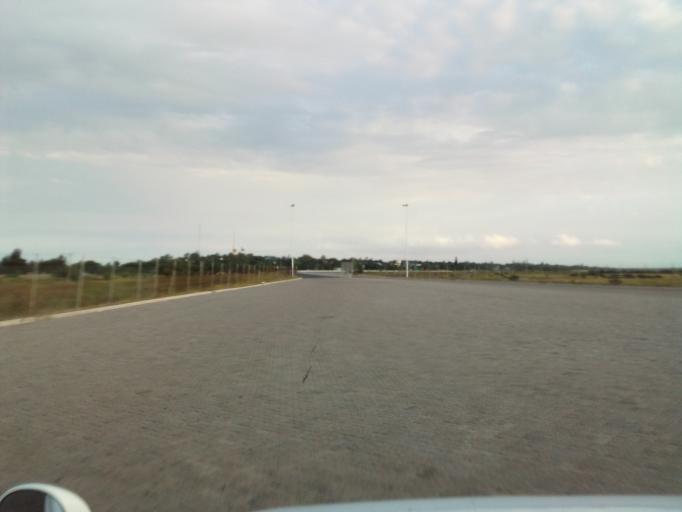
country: MZ
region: Maputo City
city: Maputo
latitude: -25.9966
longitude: 32.5565
